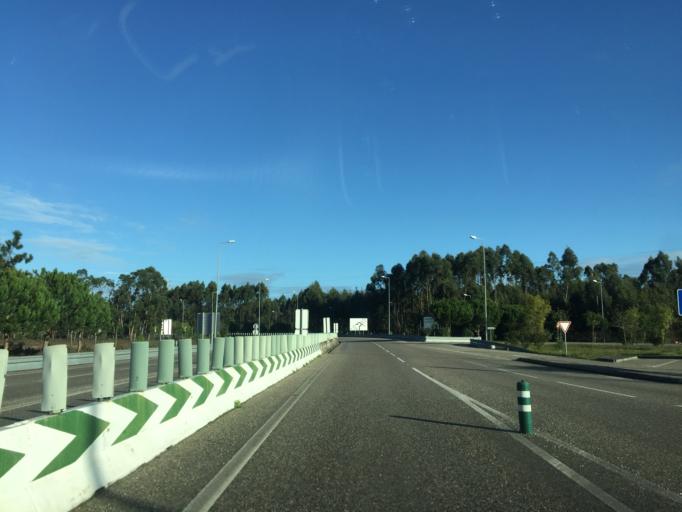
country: PT
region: Coimbra
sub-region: Figueira da Foz
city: Lavos
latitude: 40.0478
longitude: -8.8145
